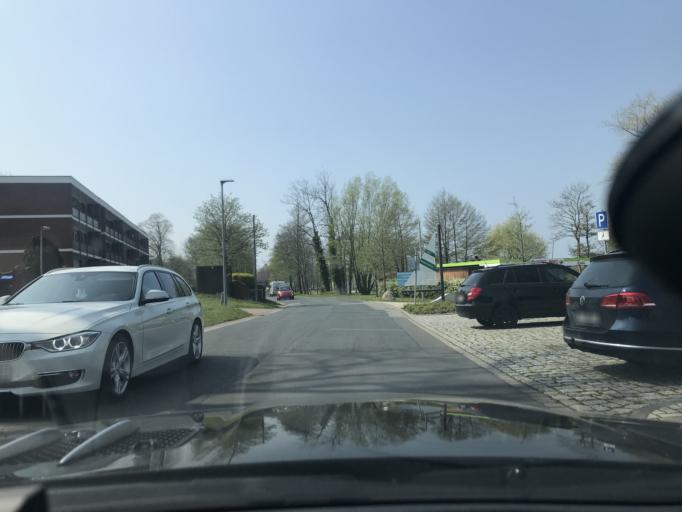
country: DE
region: Schleswig-Holstein
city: Heiligenhafen
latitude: 54.3743
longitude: 10.9718
